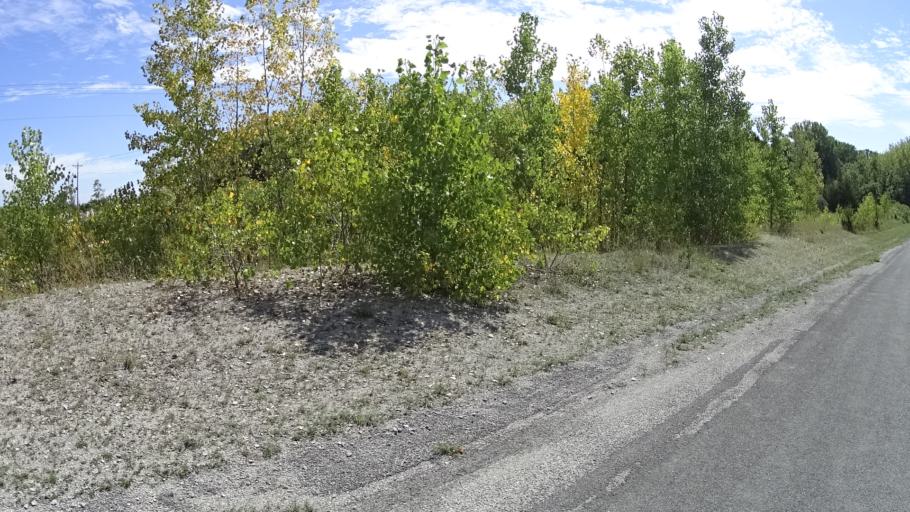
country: US
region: Ohio
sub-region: Erie County
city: Sandusky
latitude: 41.6011
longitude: -82.7211
